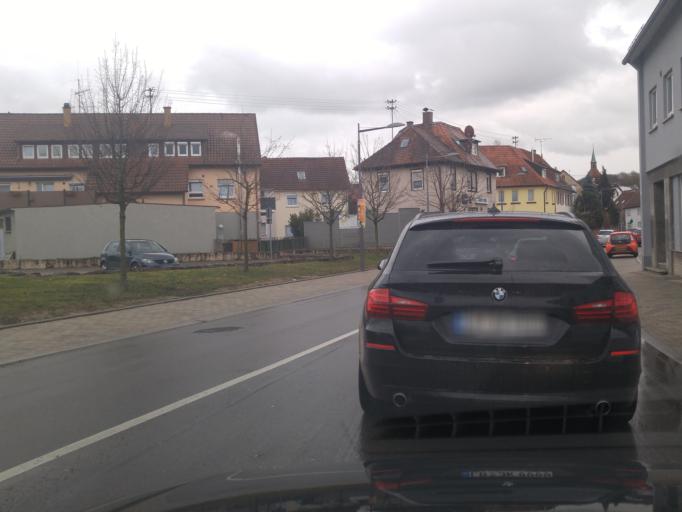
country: DE
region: Baden-Wuerttemberg
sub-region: Regierungsbezirk Stuttgart
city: Steinheim am der Murr
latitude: 48.9671
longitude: 9.2761
